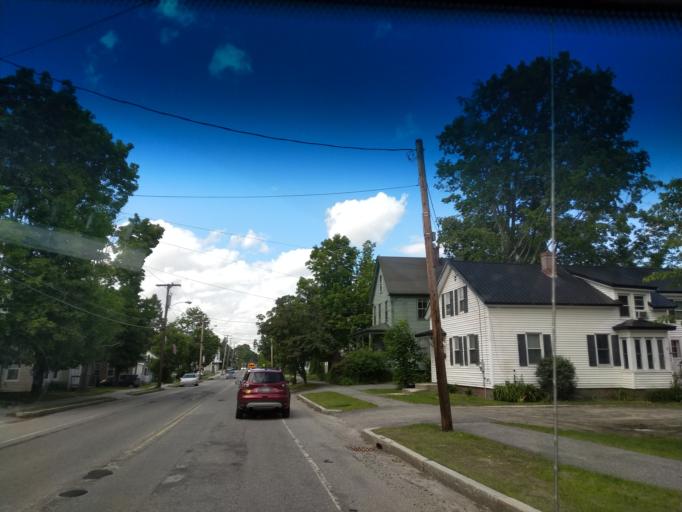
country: US
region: Maine
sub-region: Cumberland County
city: South Windham
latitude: 43.7306
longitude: -70.4255
